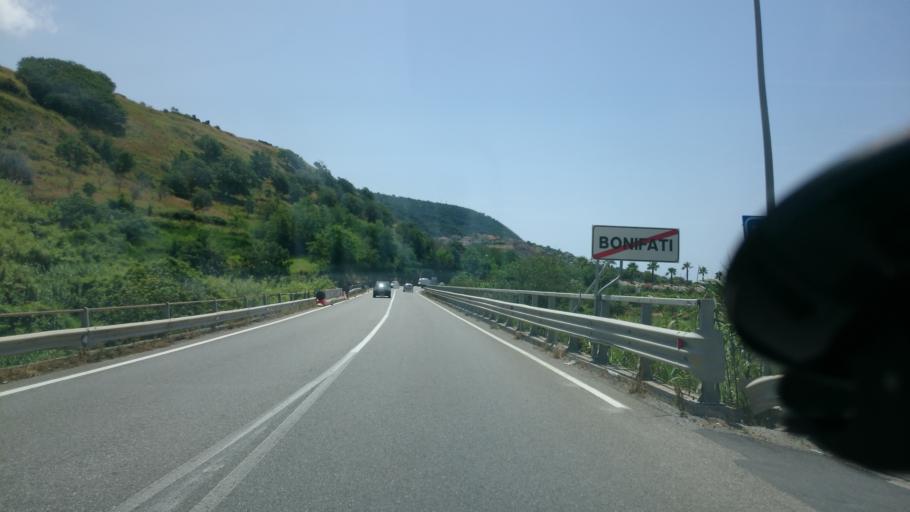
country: IT
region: Calabria
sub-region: Provincia di Cosenza
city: Cittadella del Capo
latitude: 39.5682
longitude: 15.8733
